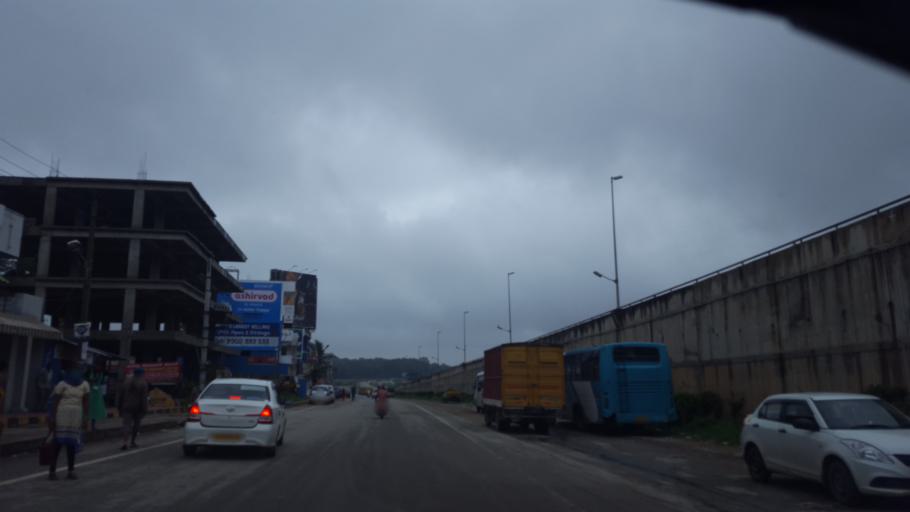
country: IN
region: Karnataka
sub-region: Bangalore Urban
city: Yelahanka
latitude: 13.1437
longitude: 77.6177
